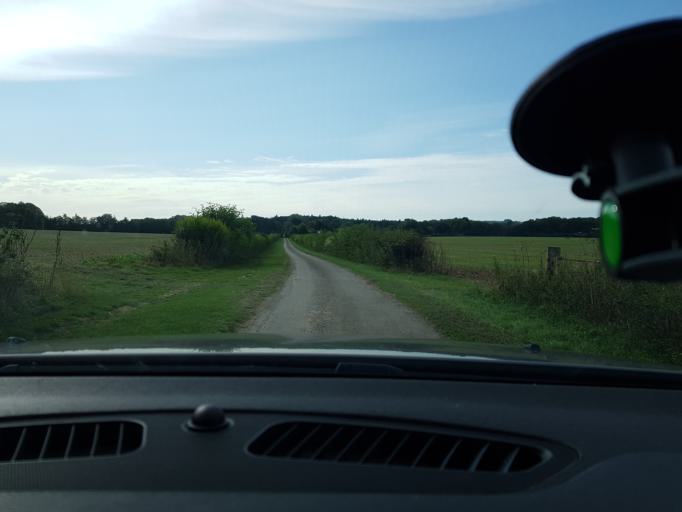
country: GB
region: England
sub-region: West Berkshire
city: Hungerford
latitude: 51.4021
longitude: -1.4843
